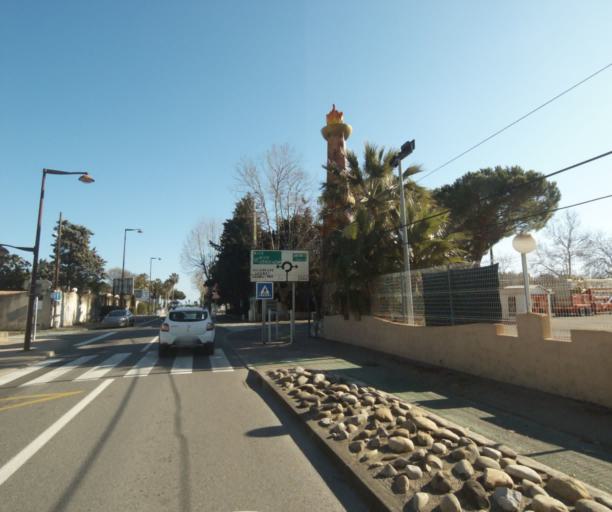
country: FR
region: Provence-Alpes-Cote d'Azur
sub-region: Departement des Alpes-Maritimes
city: Biot
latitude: 43.6130
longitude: 7.1242
